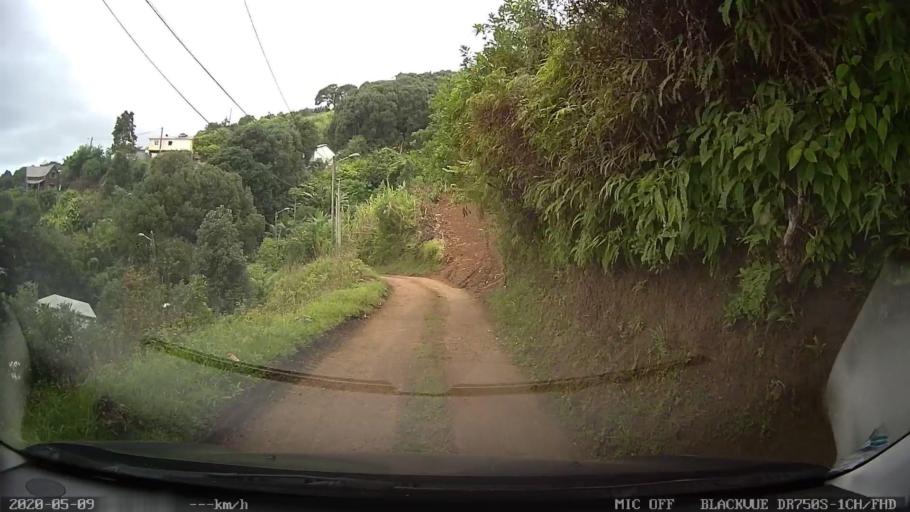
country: RE
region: Reunion
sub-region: Reunion
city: Sainte-Marie
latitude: -20.9500
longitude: 55.5294
